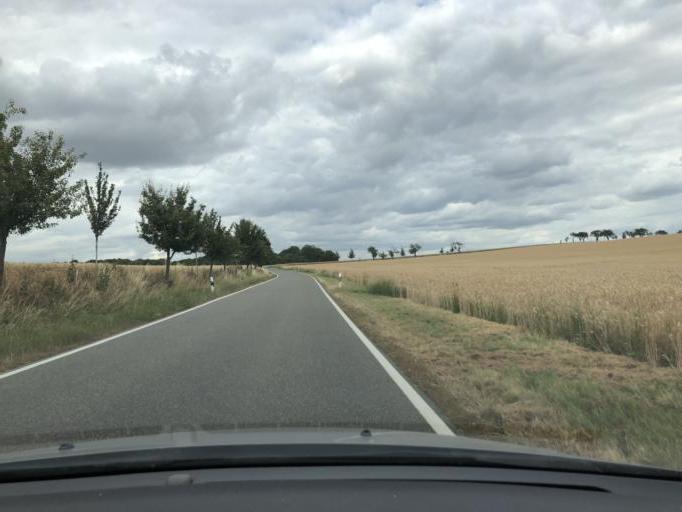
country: DE
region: Thuringia
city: Langenleuba-Niederhain
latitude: 51.0170
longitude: 12.6213
